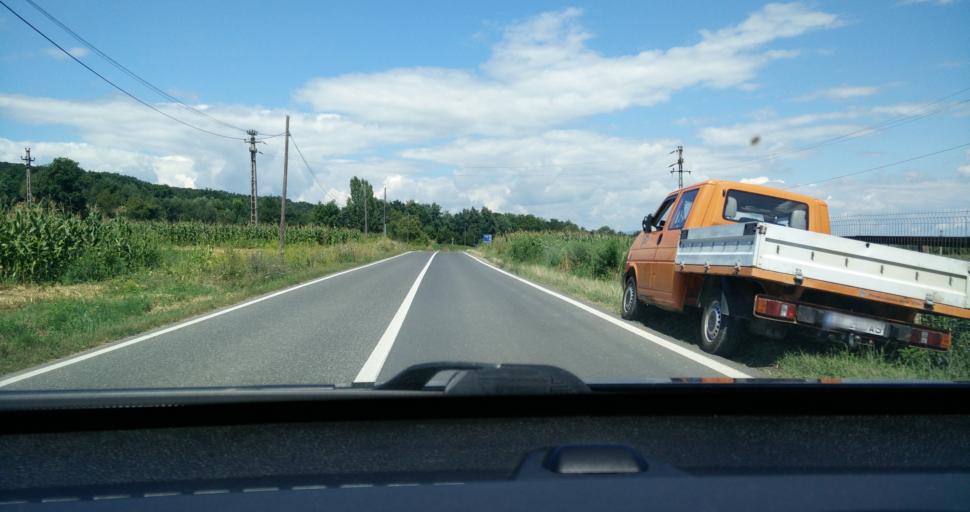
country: RO
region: Alba
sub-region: Comuna Sasciori
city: Sebesel
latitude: 45.8938
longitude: 23.5607
